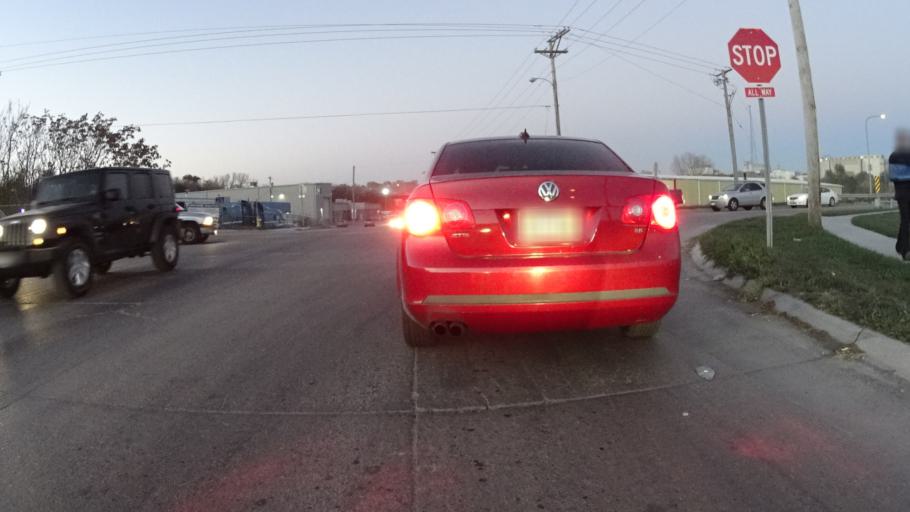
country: US
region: Nebraska
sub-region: Douglas County
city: Omaha
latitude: 41.2195
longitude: -95.9601
